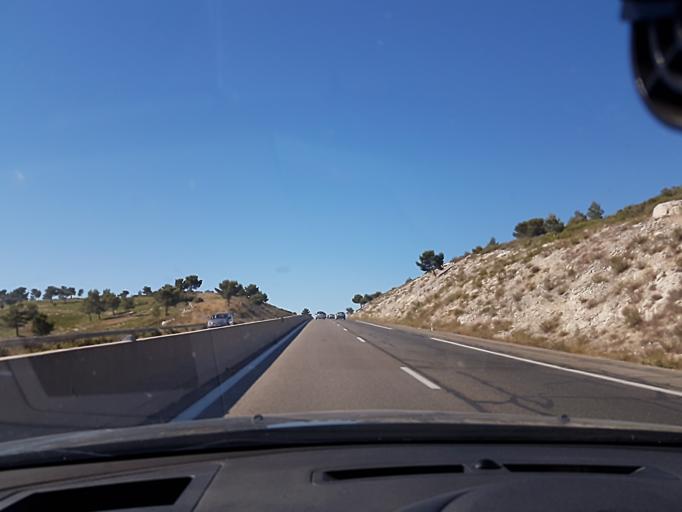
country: FR
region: Provence-Alpes-Cote d'Azur
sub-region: Departement des Bouches-du-Rhone
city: Carry-le-Rouet
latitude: 43.3471
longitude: 5.1697
